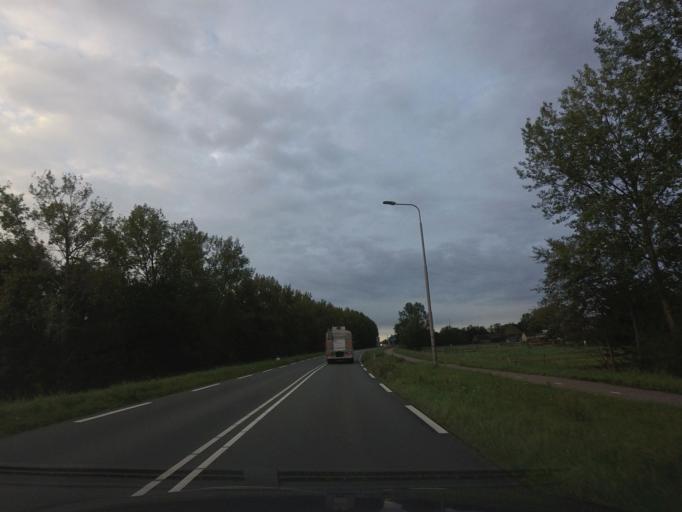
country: NL
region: North Holland
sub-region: Gemeente Zaanstad
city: Zaanstad
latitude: 52.5175
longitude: 4.7842
